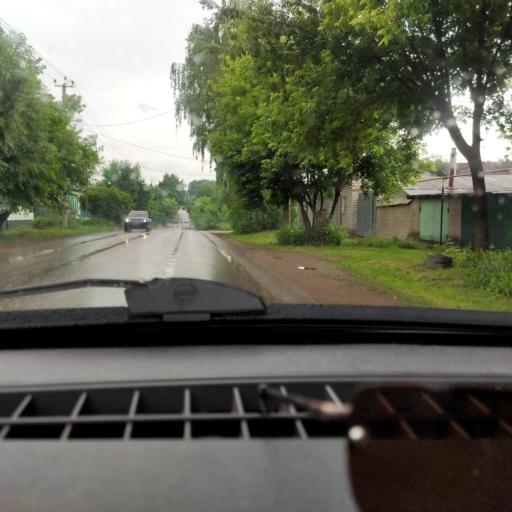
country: RU
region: Bashkortostan
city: Birsk
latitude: 55.4173
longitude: 55.5420
